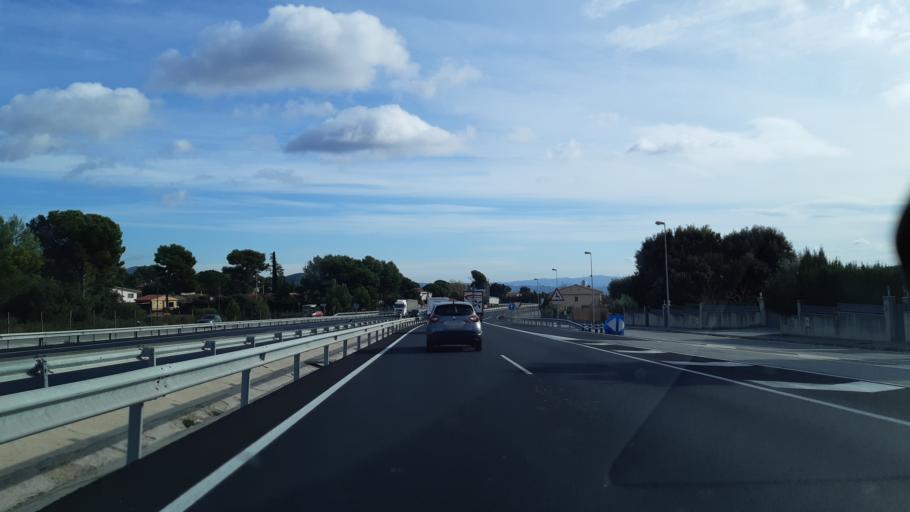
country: ES
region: Catalonia
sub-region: Provincia de Barcelona
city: Collbato
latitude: 41.5678
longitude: 1.8061
